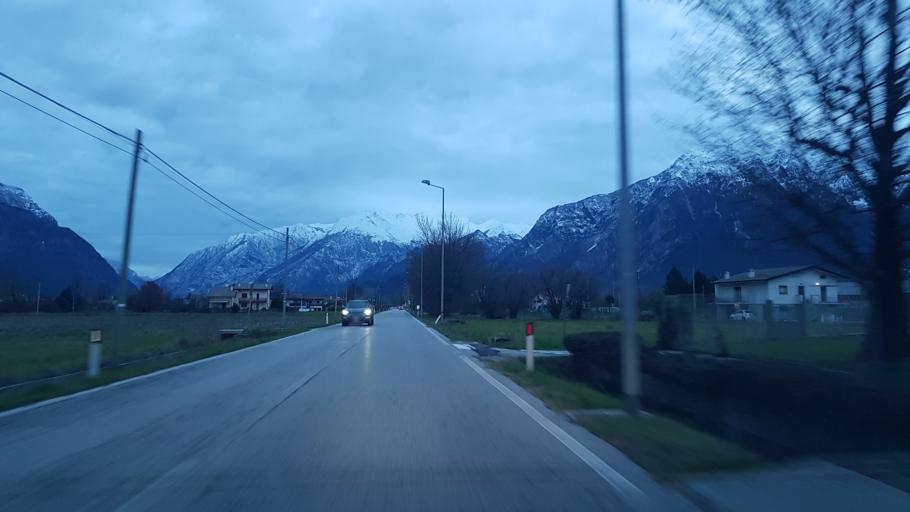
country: IT
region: Friuli Venezia Giulia
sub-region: Provincia di Udine
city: Osoppo
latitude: 46.2720
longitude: 13.0962
